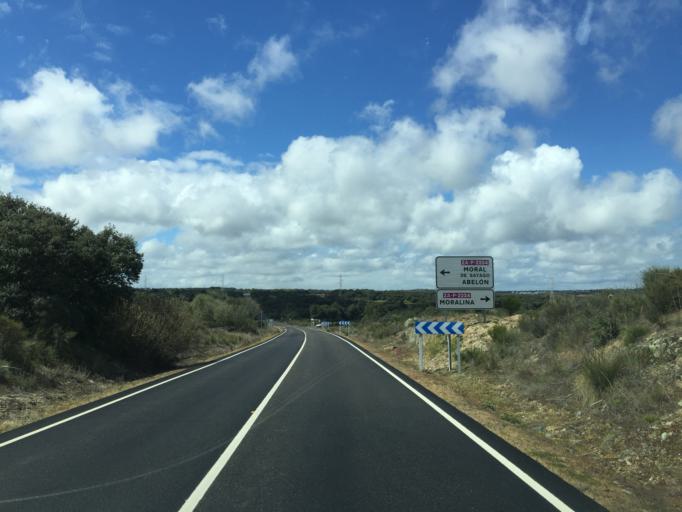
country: ES
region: Castille and Leon
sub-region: Provincia de Zamora
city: Moralina
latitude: 41.4829
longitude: -6.1220
